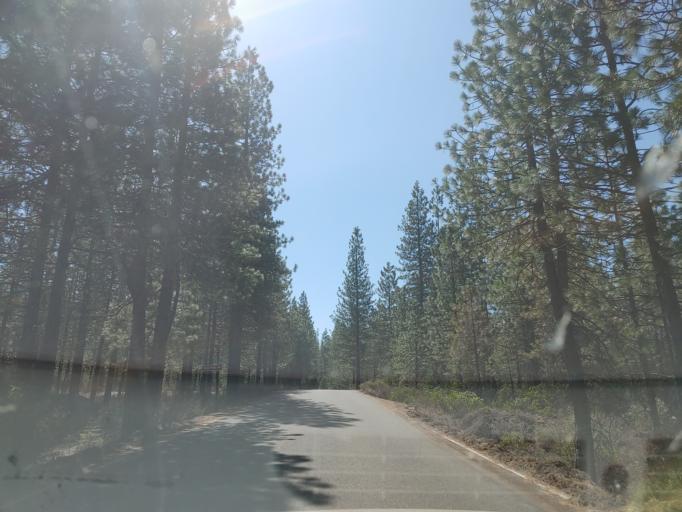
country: US
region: California
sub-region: Siskiyou County
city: McCloud
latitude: 41.2392
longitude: -122.0060
